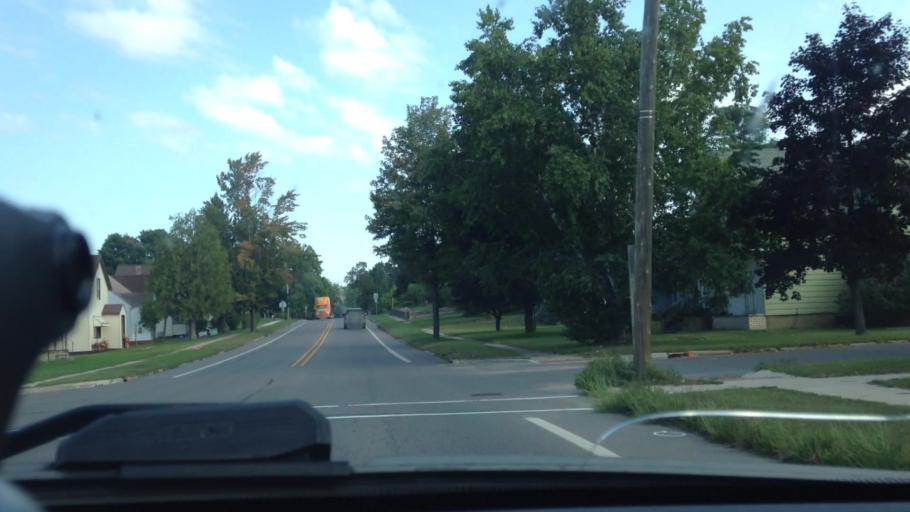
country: US
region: Michigan
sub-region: Dickinson County
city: Norway
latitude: 45.7822
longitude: -87.9098
